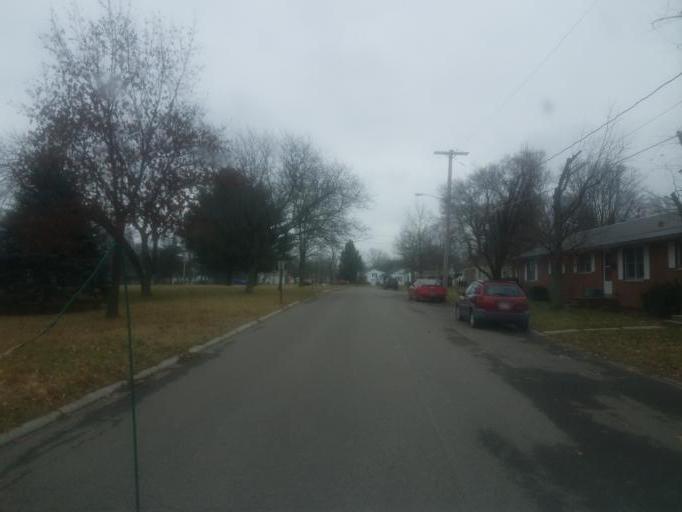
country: US
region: Ohio
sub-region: Crawford County
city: Galion
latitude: 40.7431
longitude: -82.7915
